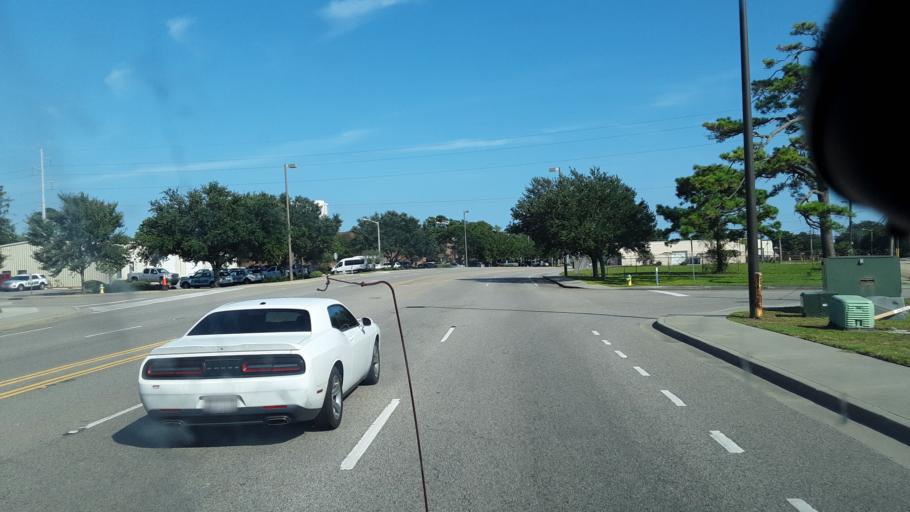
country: US
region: South Carolina
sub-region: Horry County
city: Myrtle Beach
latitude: 33.6982
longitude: -78.8842
